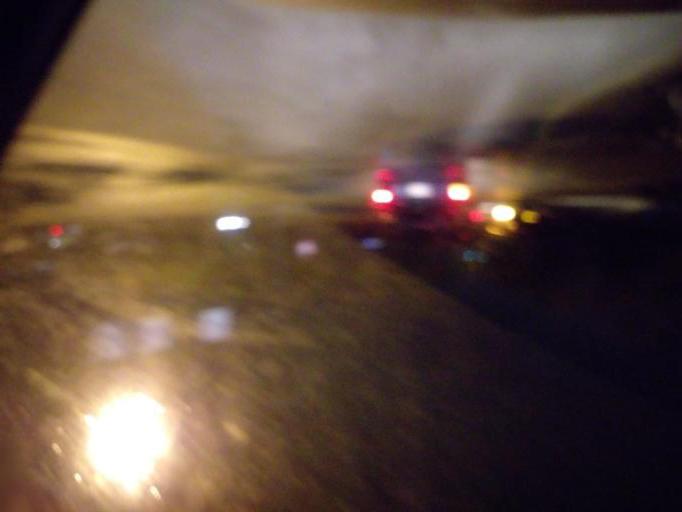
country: TR
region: Ankara
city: Batikent
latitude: 39.8961
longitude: 32.7335
